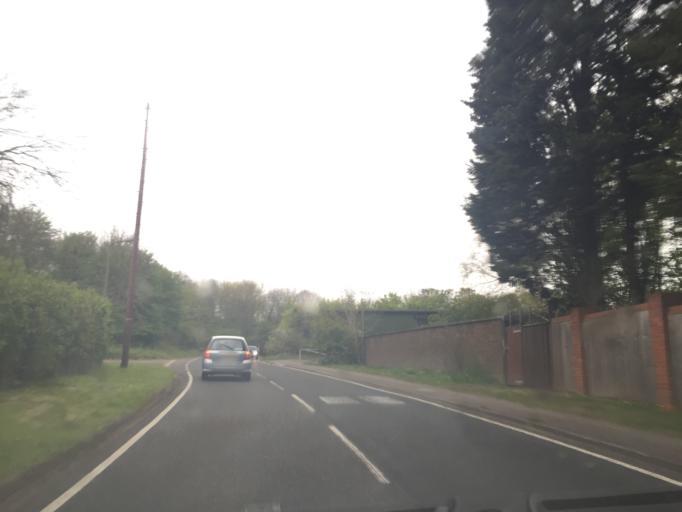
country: GB
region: England
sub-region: Essex
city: Theydon Bois
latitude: 51.6883
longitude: 0.0969
